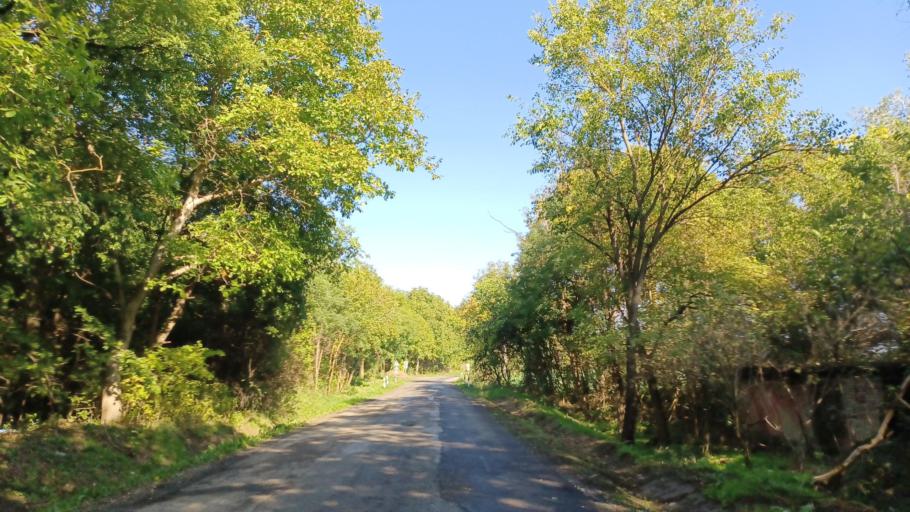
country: HU
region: Tolna
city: Nagydorog
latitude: 46.5738
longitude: 18.5905
